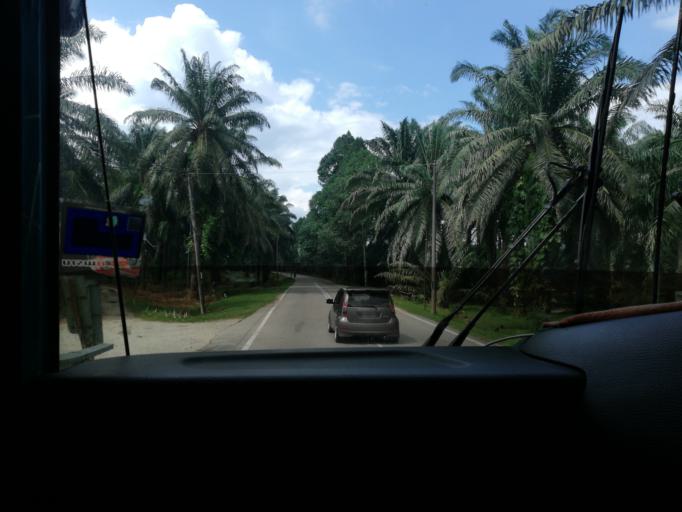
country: MY
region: Kedah
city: Kulim
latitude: 5.2408
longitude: 100.6013
